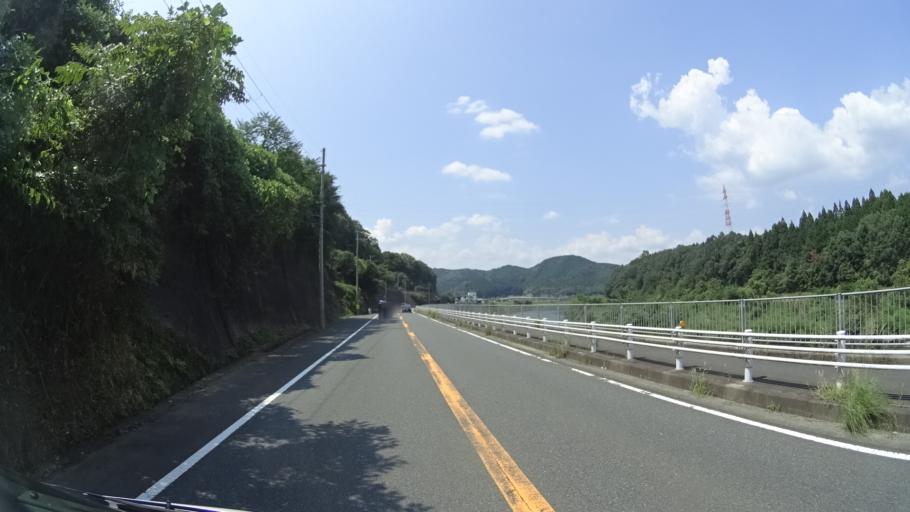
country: JP
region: Kyoto
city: Fukuchiyama
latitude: 35.2724
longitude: 135.1443
